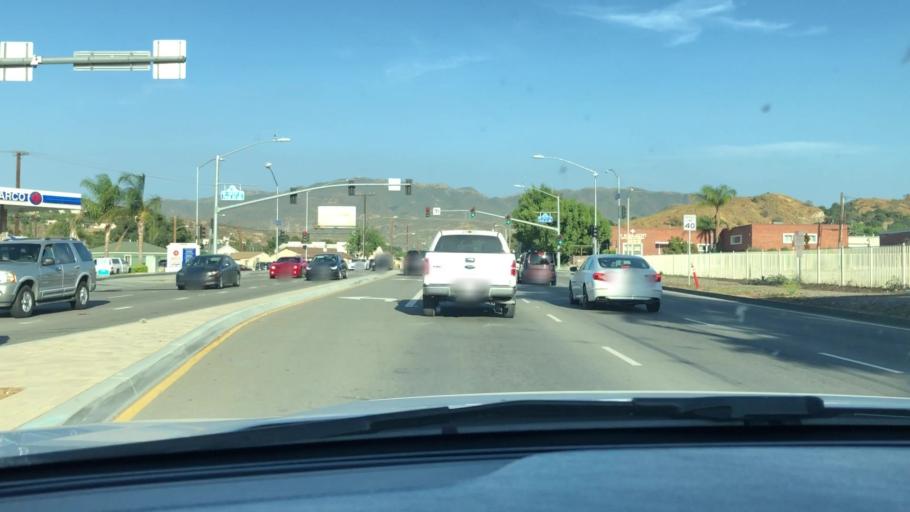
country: US
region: California
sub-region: Los Angeles County
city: Santa Clarita
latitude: 34.3749
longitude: -118.5228
